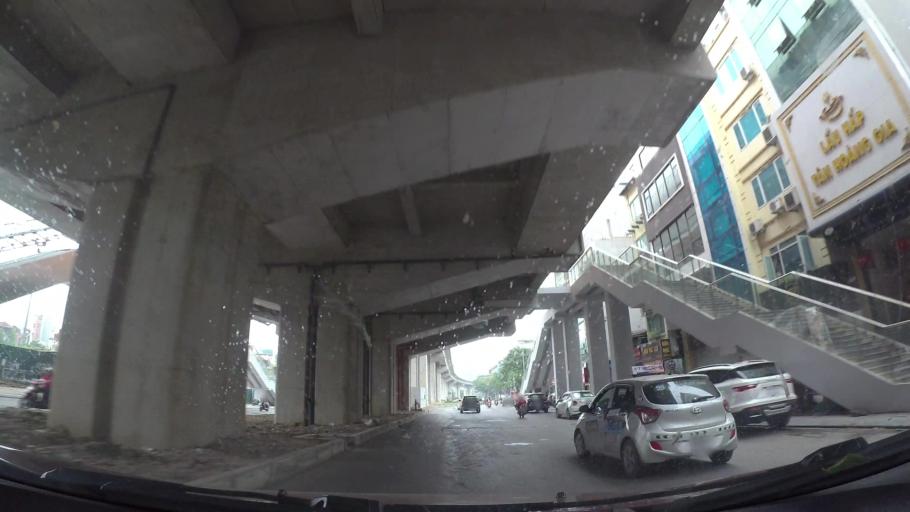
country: VN
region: Ha Noi
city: Dong Da
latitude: 21.0146
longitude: 105.8199
